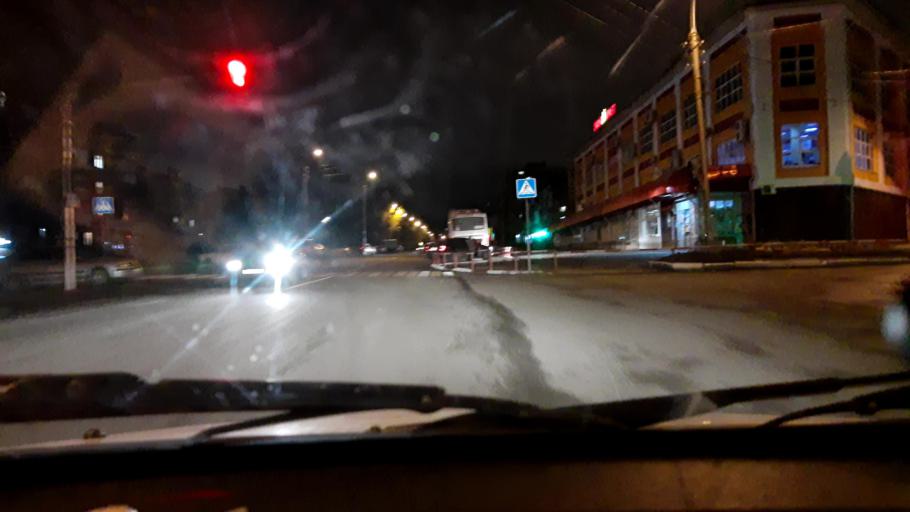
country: RU
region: Bashkortostan
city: Ufa
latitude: 54.8164
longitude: 56.1254
